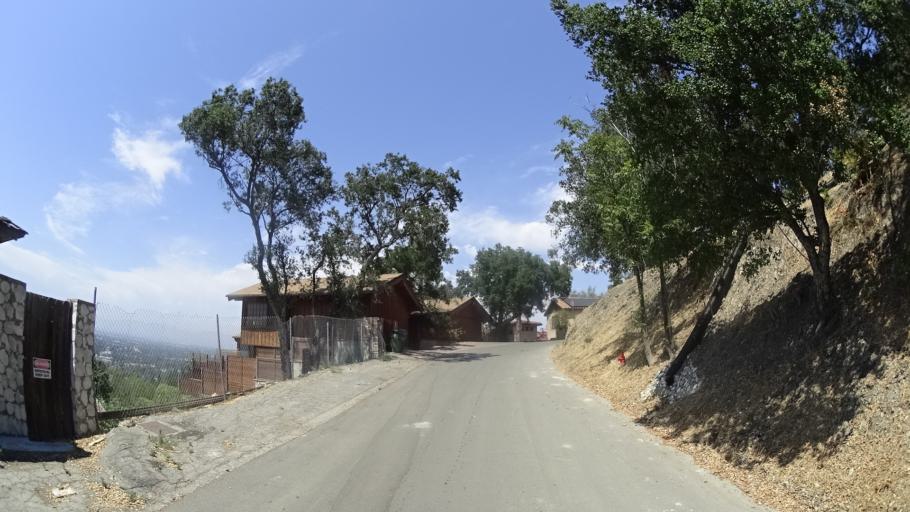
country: US
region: California
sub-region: Los Angeles County
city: Sherman Oaks
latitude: 34.1383
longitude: -118.4105
